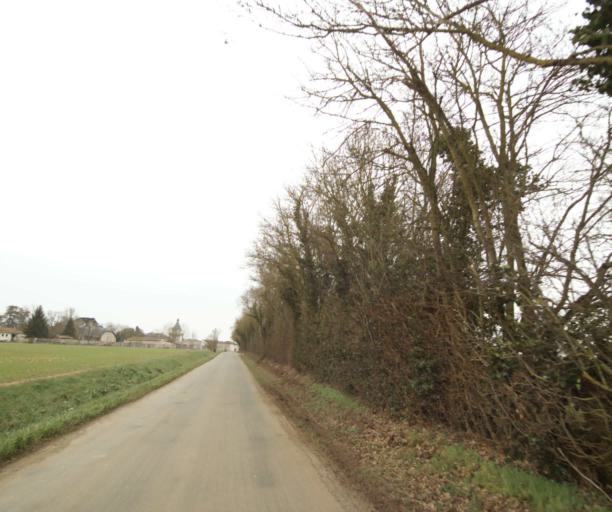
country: FR
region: Poitou-Charentes
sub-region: Departement des Deux-Sevres
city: Magne
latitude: 46.3331
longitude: -0.5204
